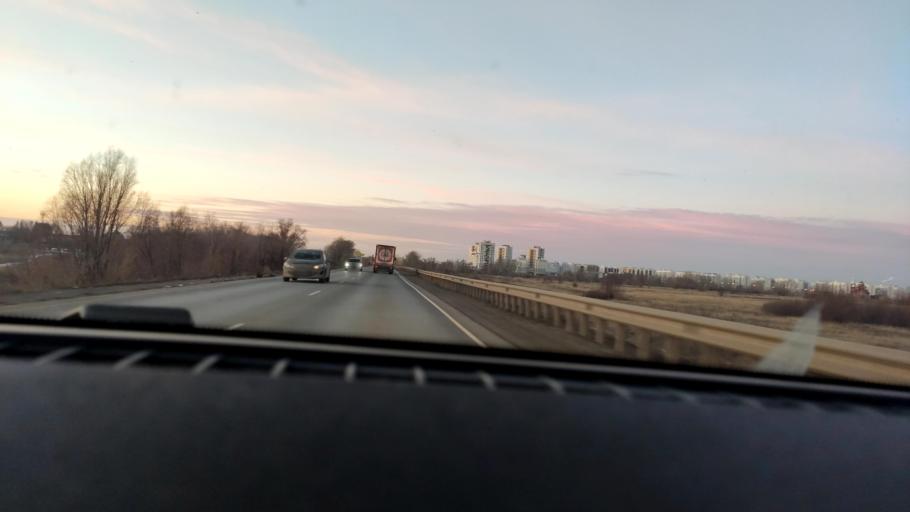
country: RU
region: Samara
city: Samara
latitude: 53.0954
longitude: 50.1464
